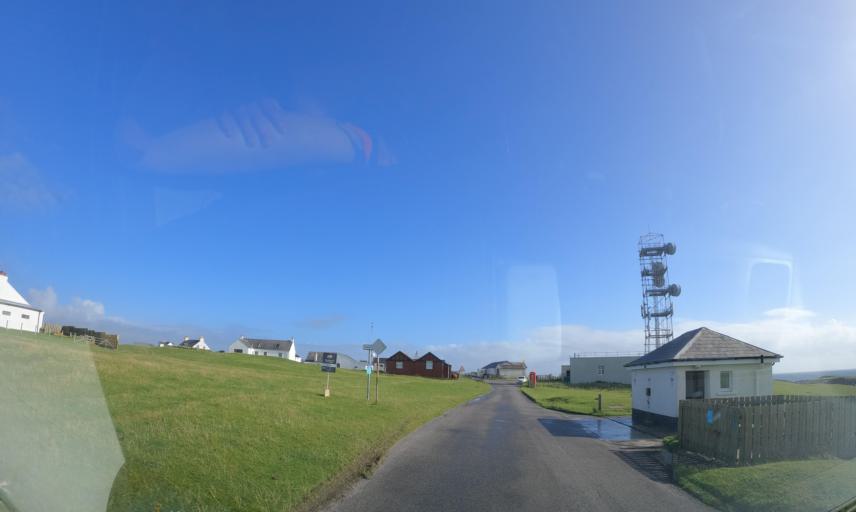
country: GB
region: Scotland
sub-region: Eilean Siar
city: Barra
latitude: 56.4997
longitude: -6.8082
